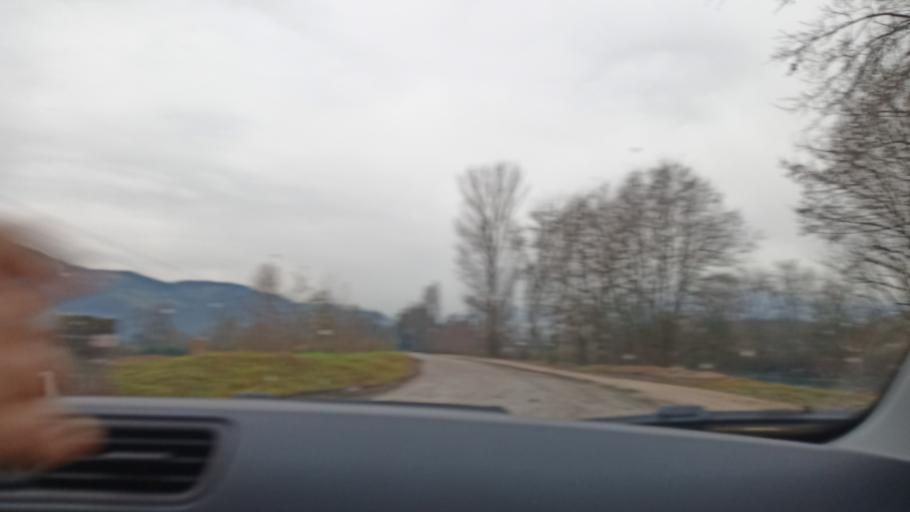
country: FR
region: Rhone-Alpes
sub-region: Departement de l'Isere
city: Domene
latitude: 45.2152
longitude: 5.8348
